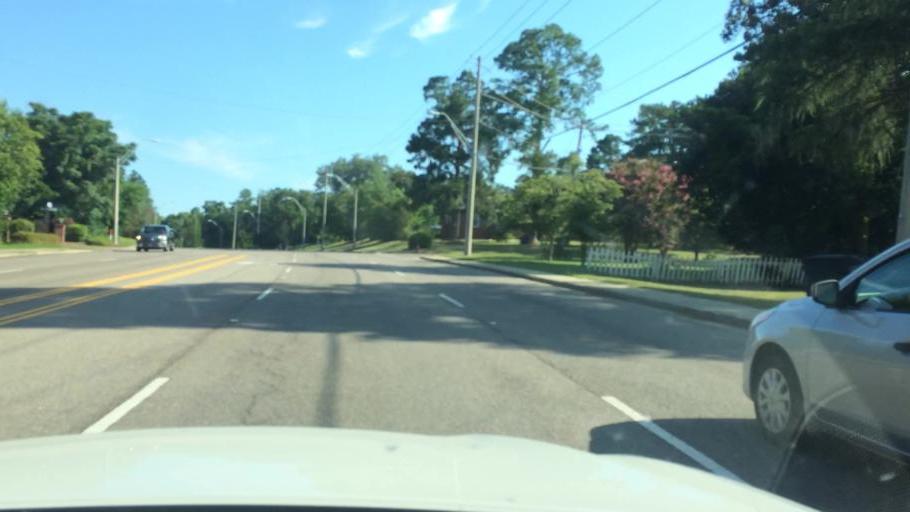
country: US
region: South Carolina
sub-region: Aiken County
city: North Augusta
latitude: 33.5254
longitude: -81.9791
